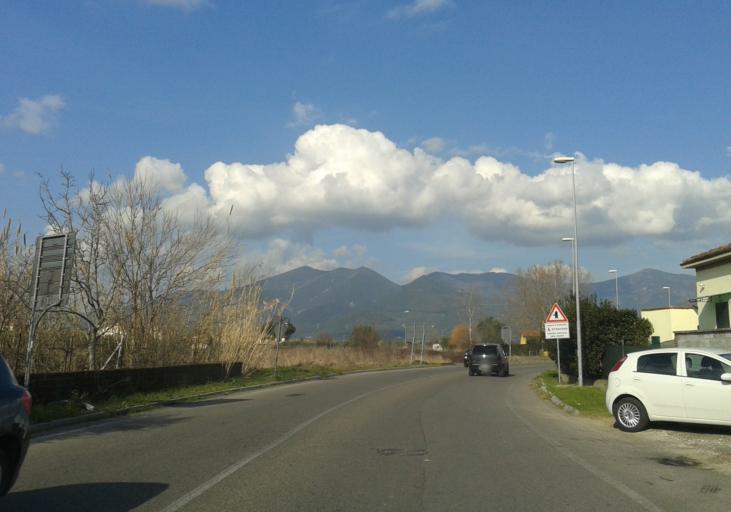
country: IT
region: Tuscany
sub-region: Province of Pisa
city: Campo
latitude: 43.6885
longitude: 10.4819
